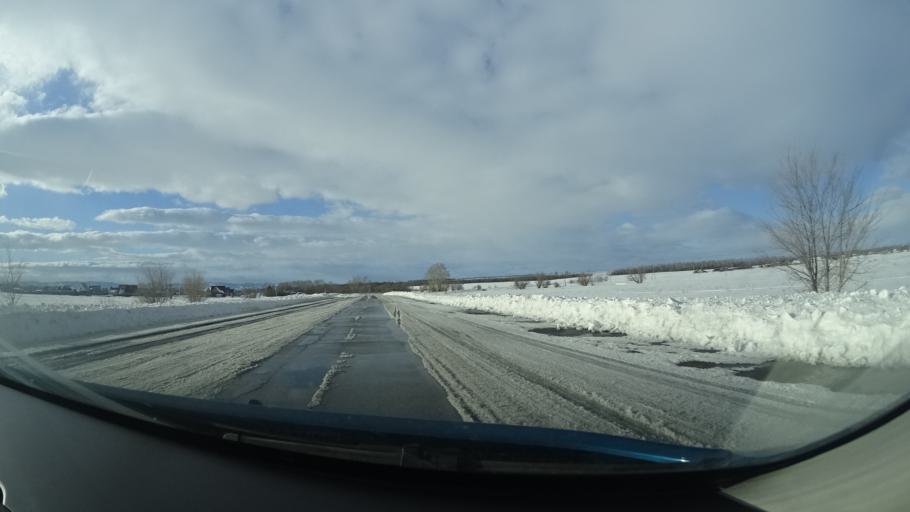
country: RU
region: Chelyabinsk
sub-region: Gorod Magnitogorsk
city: Magnitogorsk
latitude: 53.5891
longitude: 58.8781
